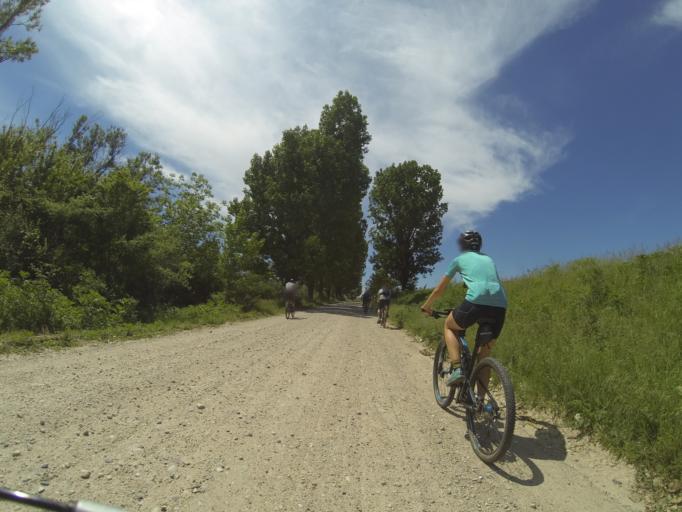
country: RO
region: Dolj
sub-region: Comuna Teslui
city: Teslui
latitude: 44.2014
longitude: 24.1408
